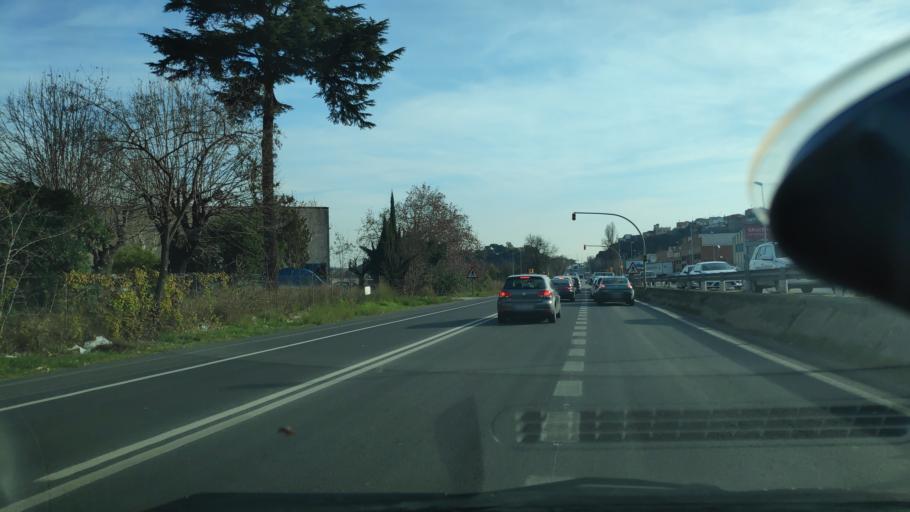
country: ES
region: Catalonia
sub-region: Provincia de Barcelona
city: Sabadell
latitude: 41.5716
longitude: 2.0956
